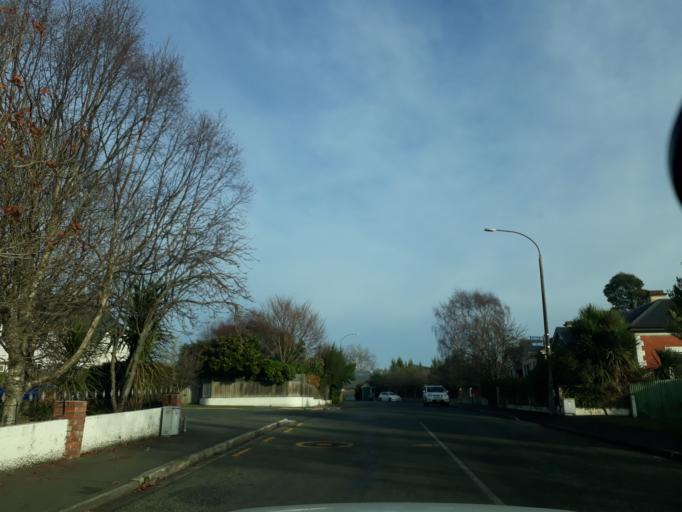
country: NZ
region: Canterbury
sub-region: Timaru District
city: Timaru
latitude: -44.3879
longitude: 171.2405
